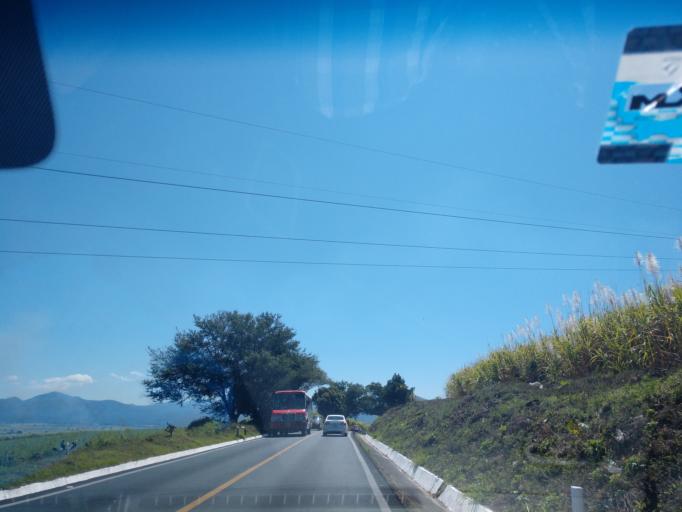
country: MX
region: Nayarit
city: Xalisco
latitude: 21.3890
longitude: -104.8915
